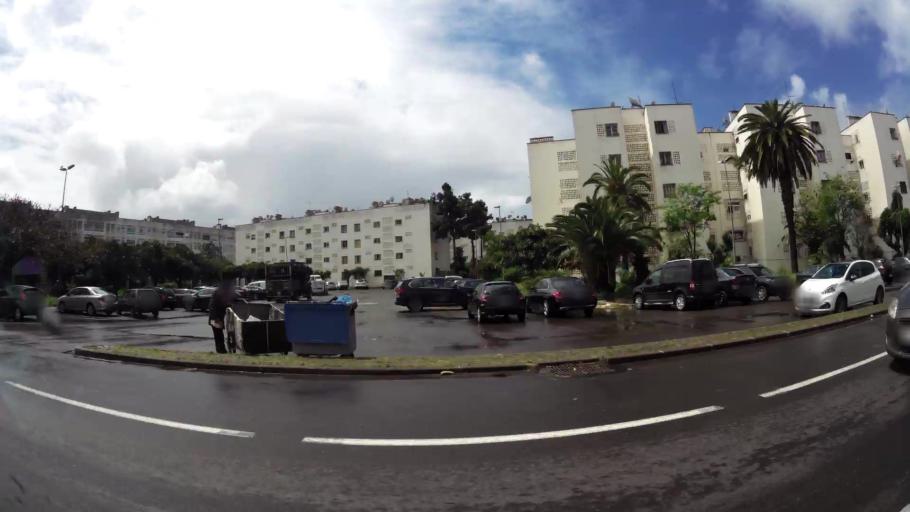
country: MA
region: Grand Casablanca
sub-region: Casablanca
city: Casablanca
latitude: 33.5664
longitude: -7.6392
